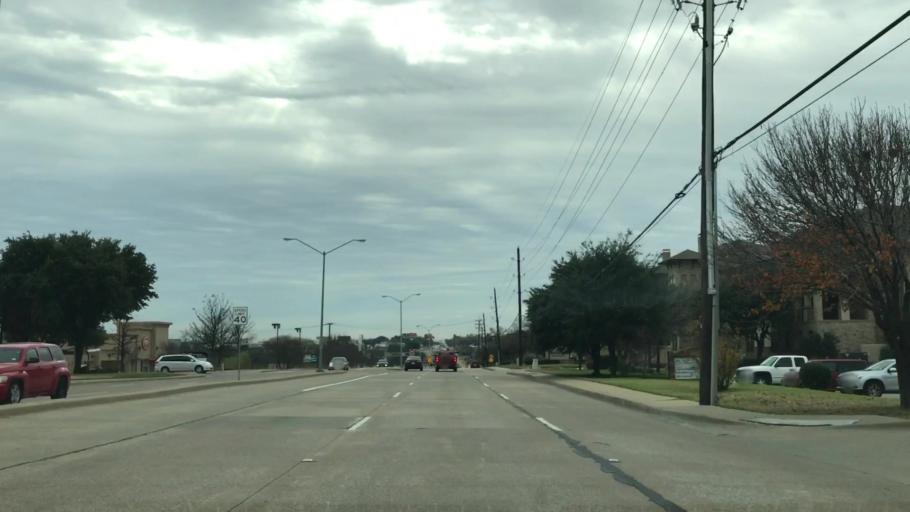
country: US
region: Texas
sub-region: Dallas County
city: Carrollton
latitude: 32.9723
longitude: -96.8900
